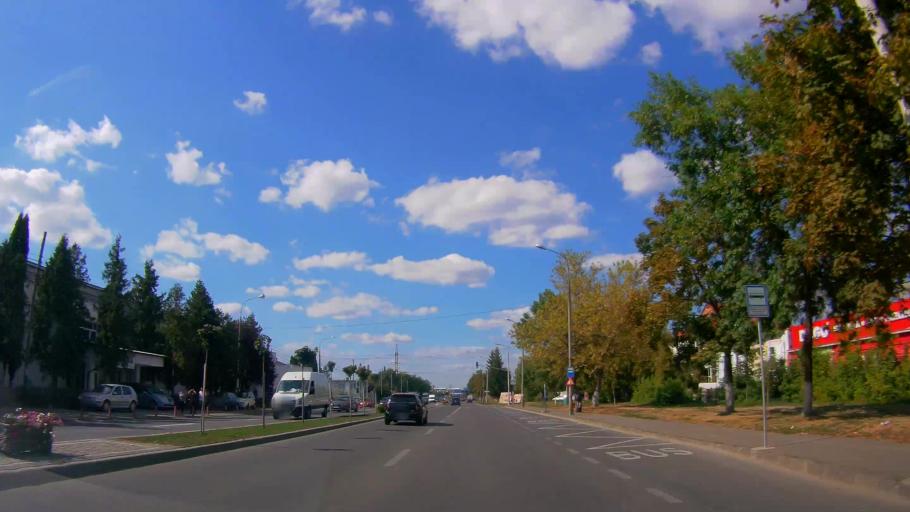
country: RO
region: Salaj
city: Zalau
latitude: 47.2039
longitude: 23.0505
